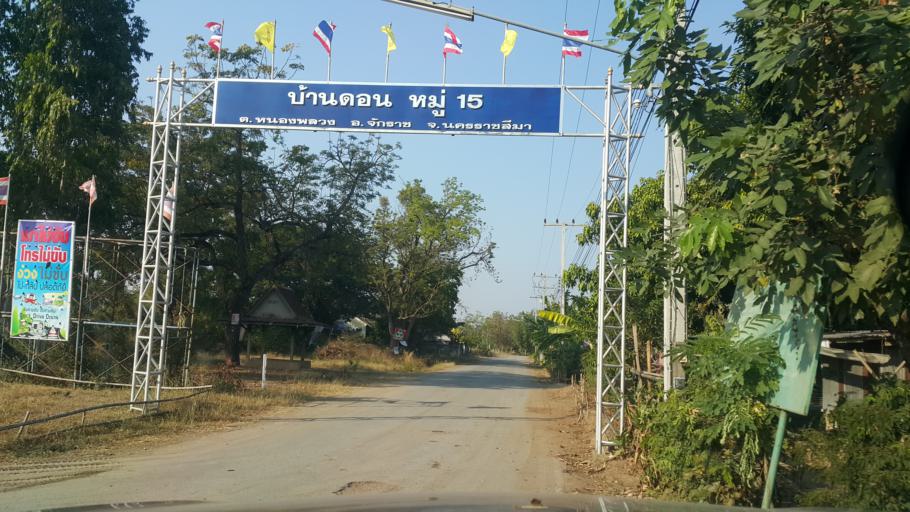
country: TH
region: Nakhon Ratchasima
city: Chakkarat
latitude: 15.0678
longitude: 102.3951
